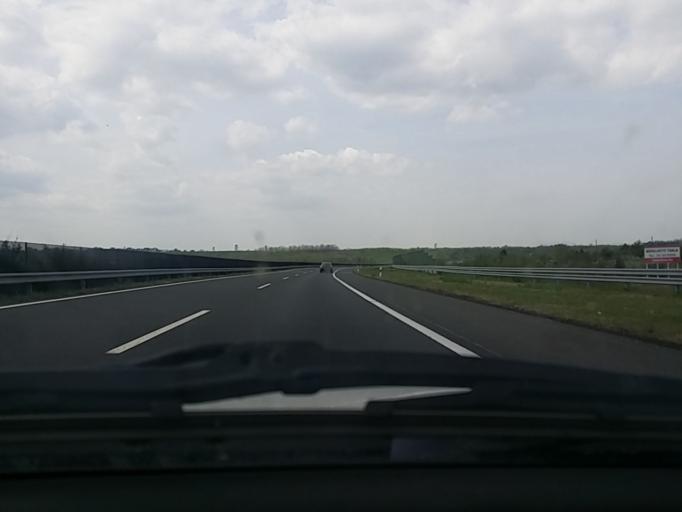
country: HU
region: Somogy
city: Balatonszarszo
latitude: 46.7902
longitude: 17.7902
